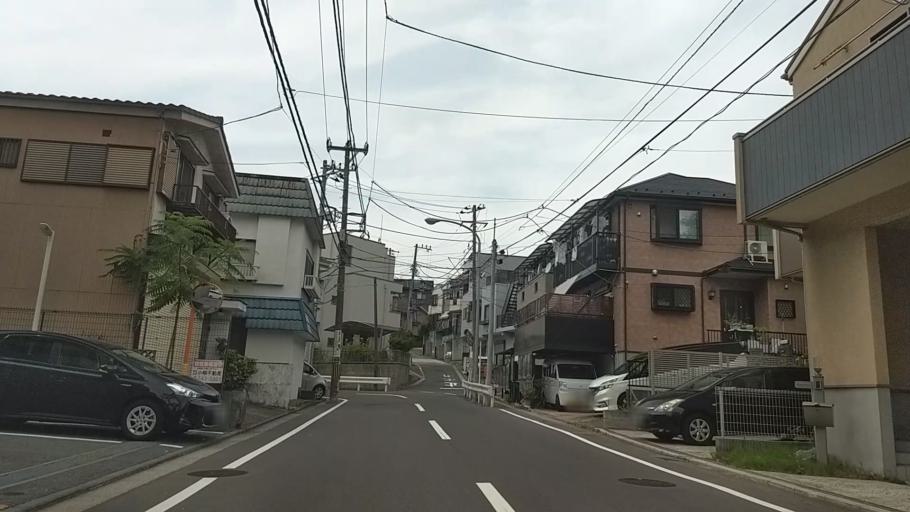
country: JP
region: Kanagawa
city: Yokohama
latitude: 35.4403
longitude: 139.6111
